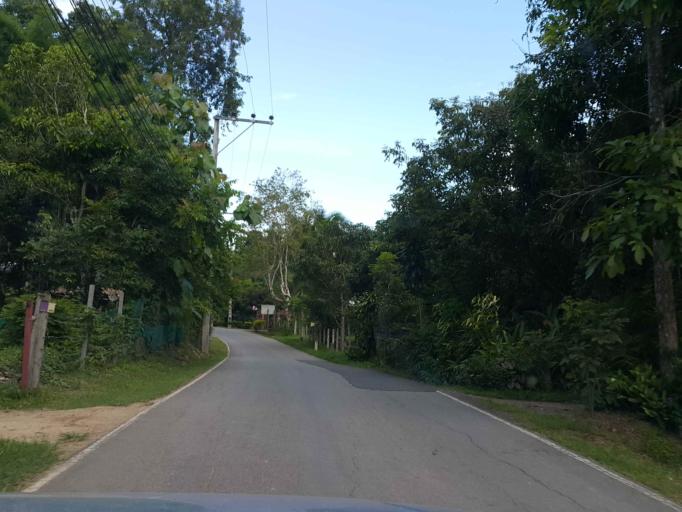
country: TH
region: Chiang Mai
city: Mae Taeng
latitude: 18.9630
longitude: 98.9134
